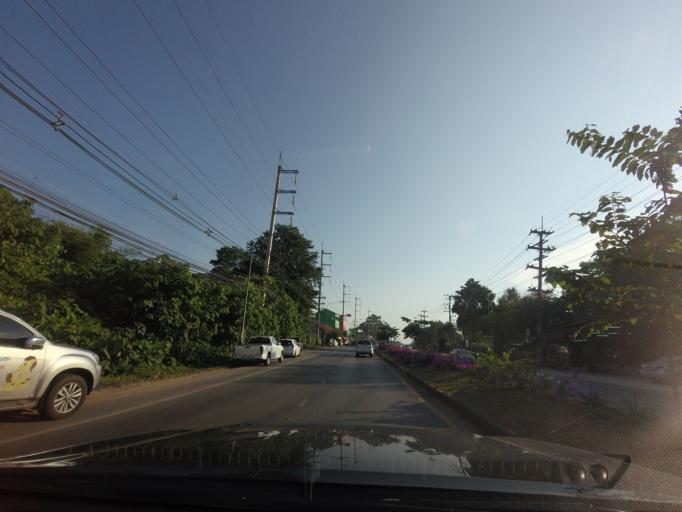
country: TH
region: Nan
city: Nan
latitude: 18.7687
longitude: 100.7644
